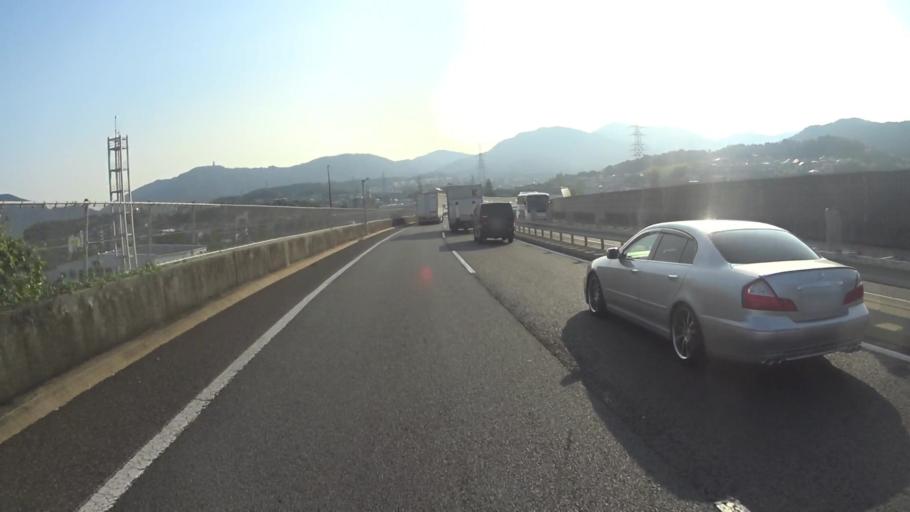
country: JP
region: Shiga Prefecture
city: Otsu-shi
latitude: 34.9571
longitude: 135.9134
